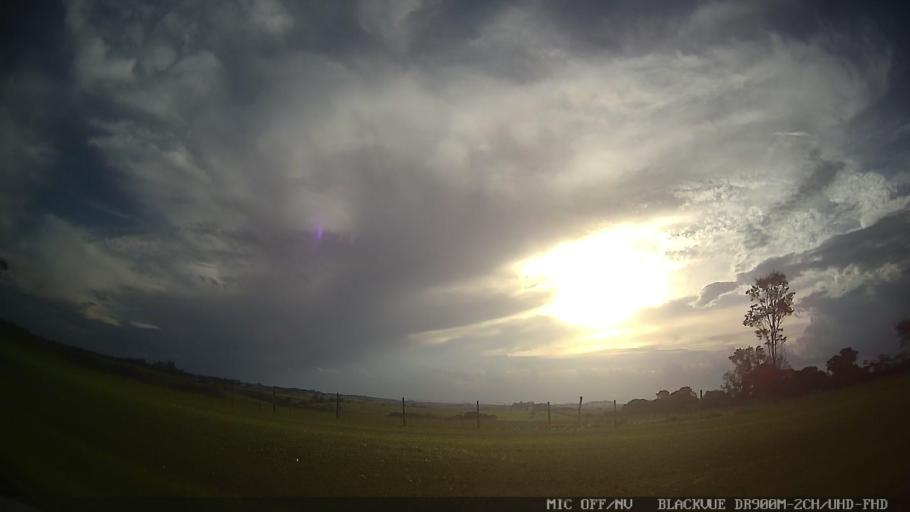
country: BR
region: Sao Paulo
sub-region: Cerquilho
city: Cerquilho
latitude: -23.1812
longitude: -47.6383
